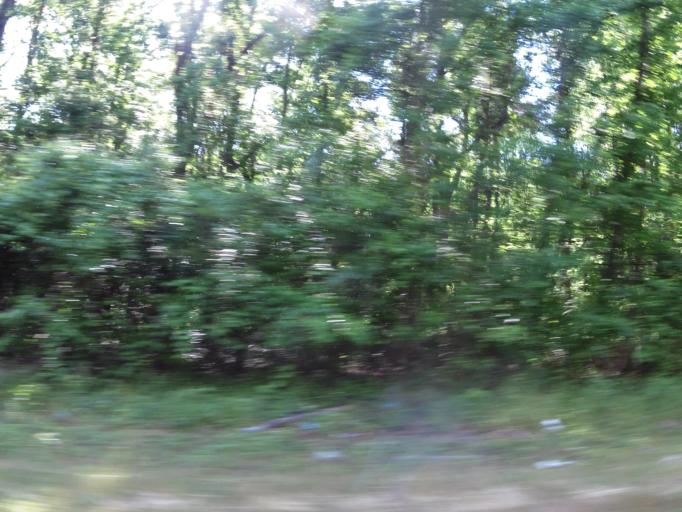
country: US
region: South Carolina
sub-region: Allendale County
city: Fairfax
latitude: 33.0558
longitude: -81.2170
